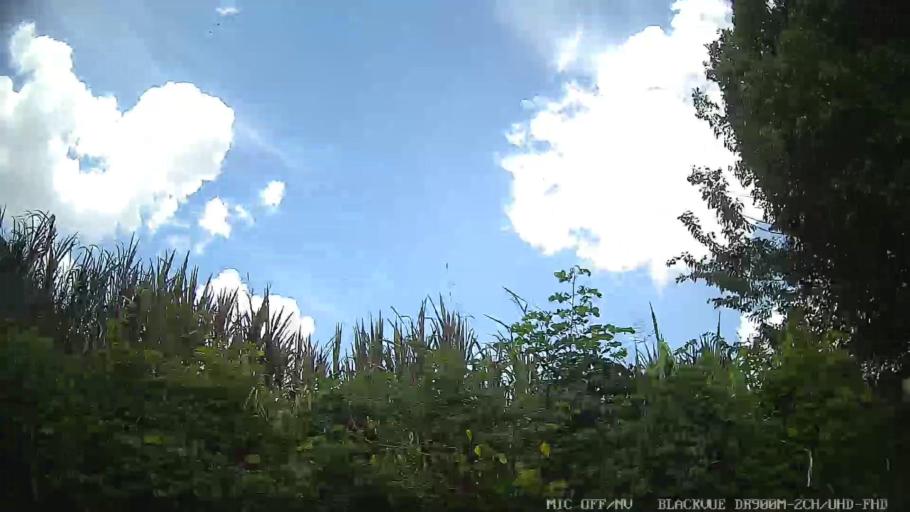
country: BR
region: Sao Paulo
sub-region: Braganca Paulista
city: Braganca Paulista
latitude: -22.9859
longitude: -46.5538
